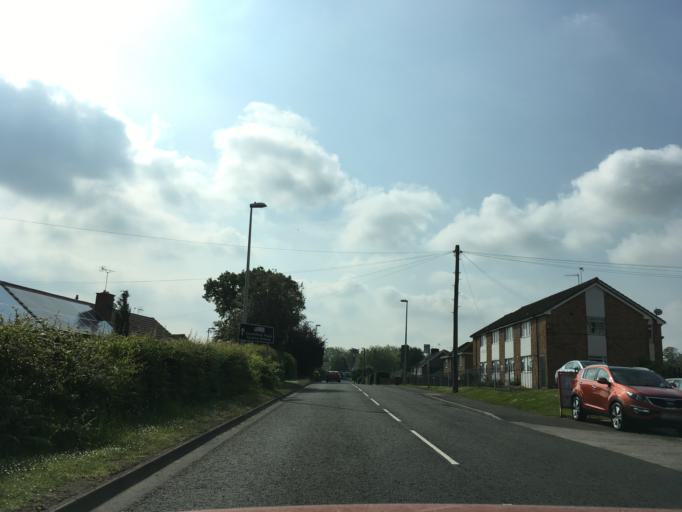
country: GB
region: England
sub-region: North Somerset
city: Nailsea
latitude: 51.4366
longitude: -2.7615
